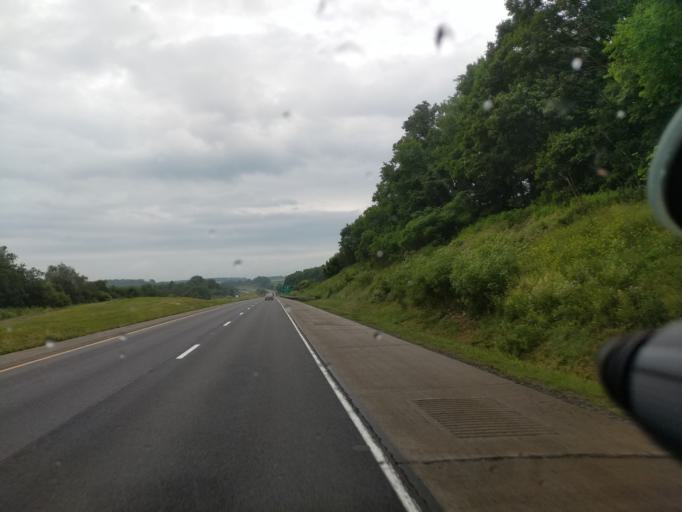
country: US
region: Pennsylvania
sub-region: Northumberland County
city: Milton
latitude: 41.0316
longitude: -76.8053
